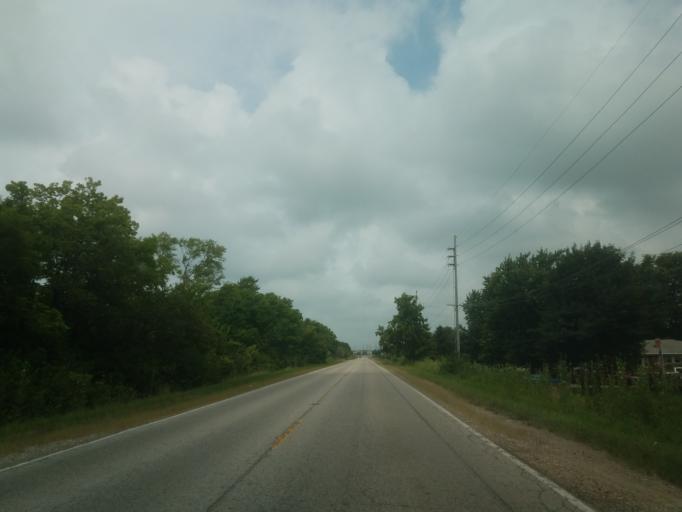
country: US
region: Illinois
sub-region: McLean County
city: Bloomington
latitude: 40.4894
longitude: -89.0165
